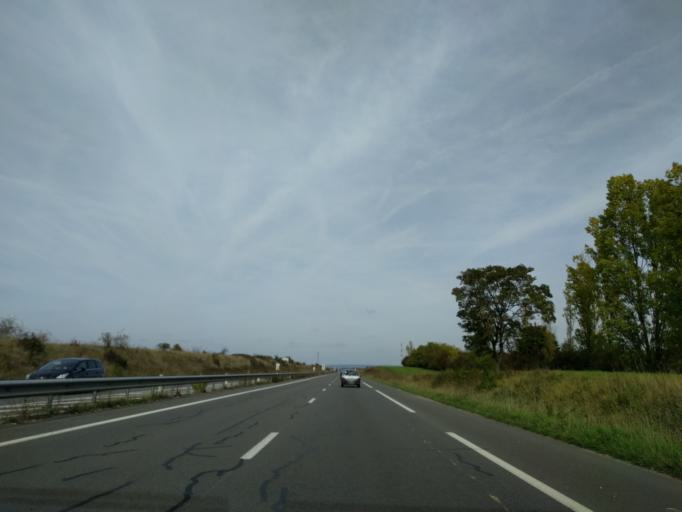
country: FR
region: Centre
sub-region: Departement du Cher
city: Bourges
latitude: 47.0725
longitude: 2.4370
